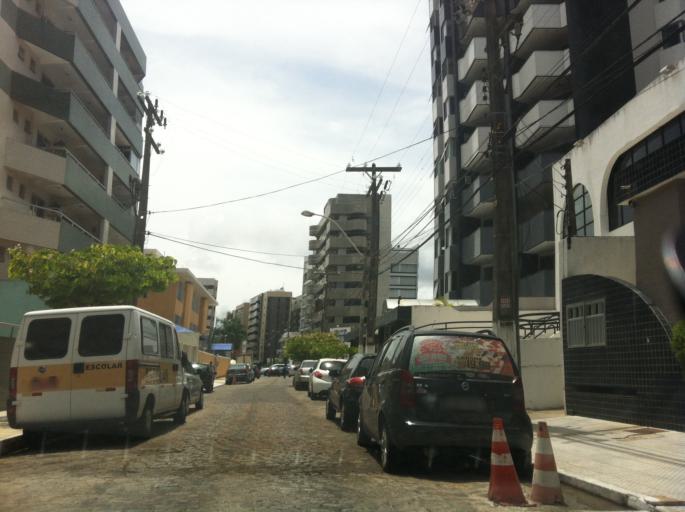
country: BR
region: Alagoas
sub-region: Maceio
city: Maceio
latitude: -9.6627
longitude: -35.7034
